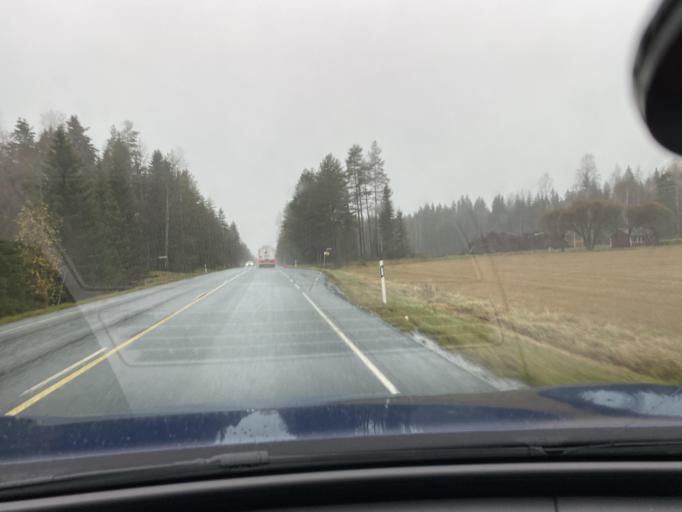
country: FI
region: Haeme
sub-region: Forssa
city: Jokioinen
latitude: 60.7873
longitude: 23.4782
